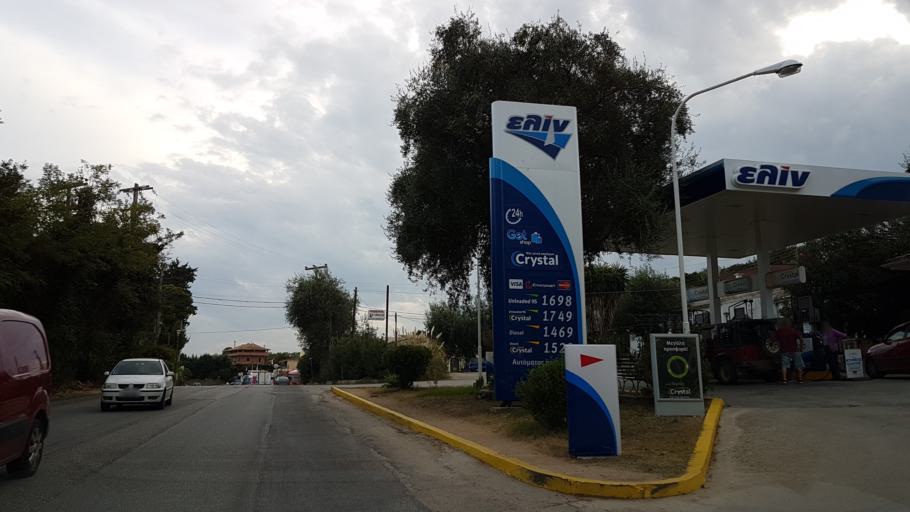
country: GR
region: Ionian Islands
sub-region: Nomos Kerkyras
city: Kontokali
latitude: 39.6754
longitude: 19.8394
